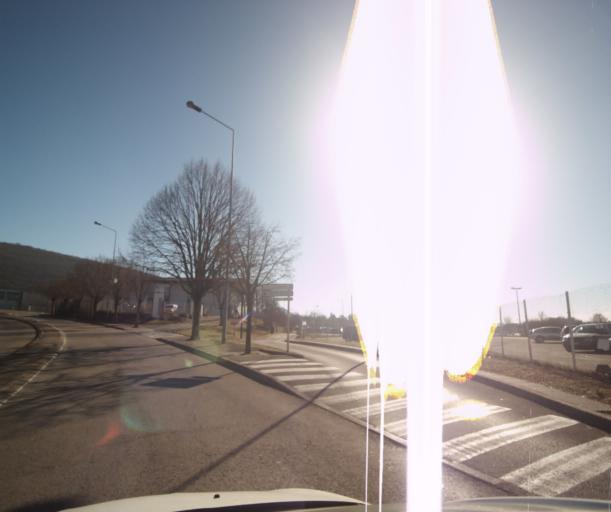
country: FR
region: Franche-Comte
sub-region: Departement du Doubs
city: Avanne-Aveney
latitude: 47.2148
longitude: 5.9673
